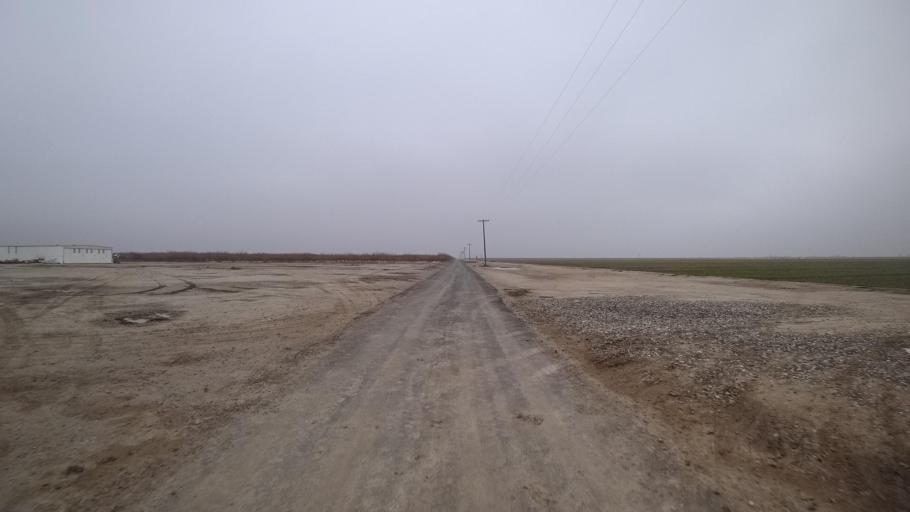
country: US
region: California
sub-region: Kern County
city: Wasco
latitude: 35.6956
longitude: -119.4907
